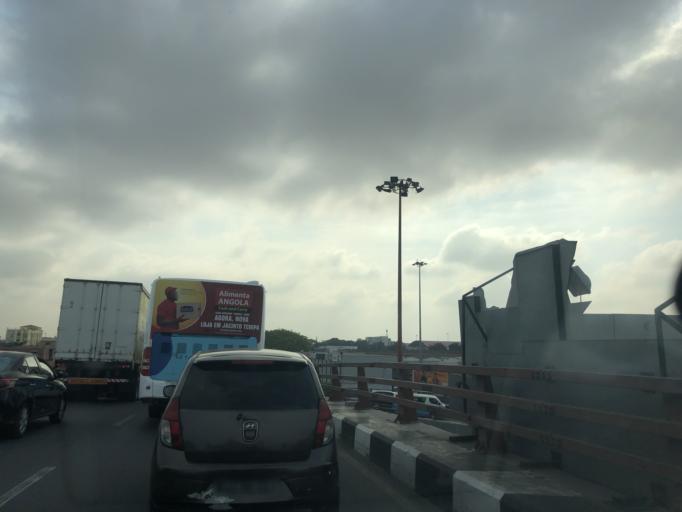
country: AO
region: Luanda
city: Luanda
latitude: -8.8457
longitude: 13.2340
